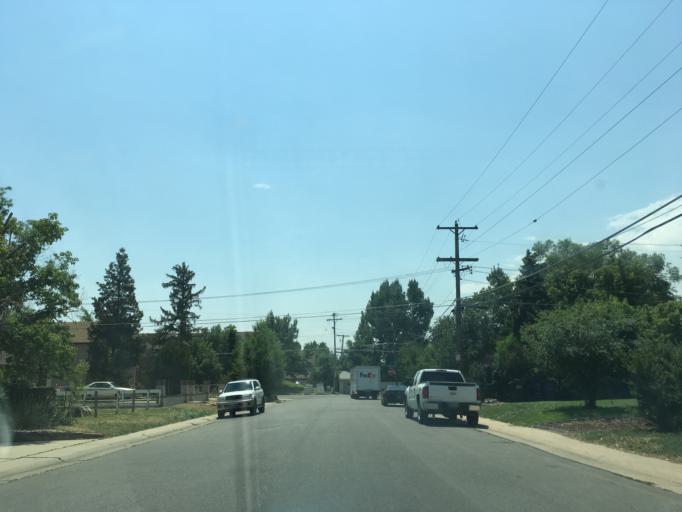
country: US
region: Colorado
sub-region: Arapahoe County
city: Sheridan
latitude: 39.6903
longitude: -105.0321
